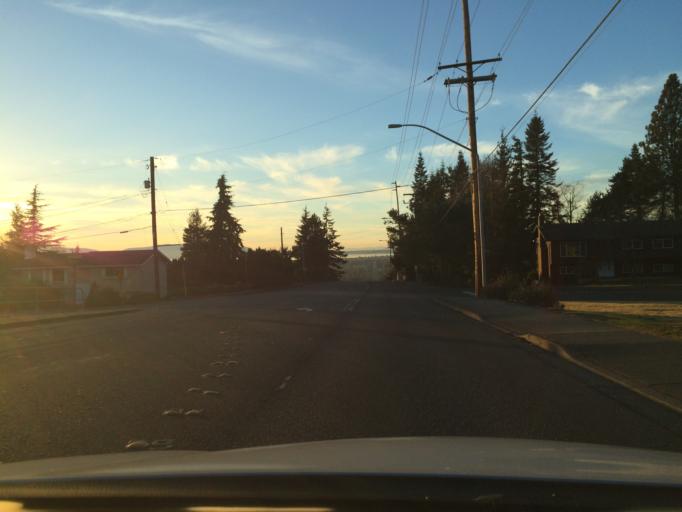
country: US
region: Washington
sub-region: Whatcom County
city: Geneva
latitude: 48.7631
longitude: -122.4263
